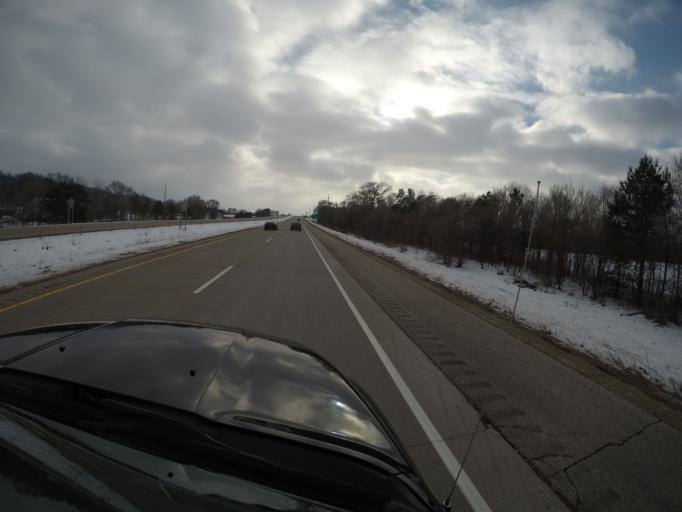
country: US
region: Wisconsin
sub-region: La Crosse County
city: Holmen
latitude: 44.0036
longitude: -91.2865
